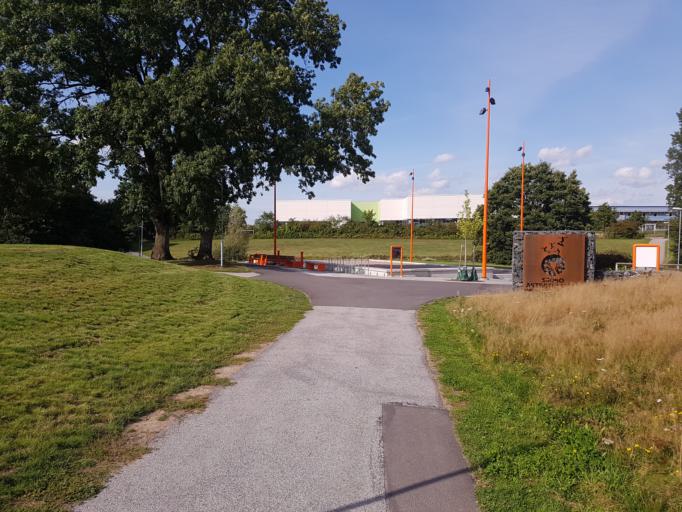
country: SE
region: Skane
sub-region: Sjobo Kommun
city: Sjoebo
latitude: 55.6352
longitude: 13.7001
